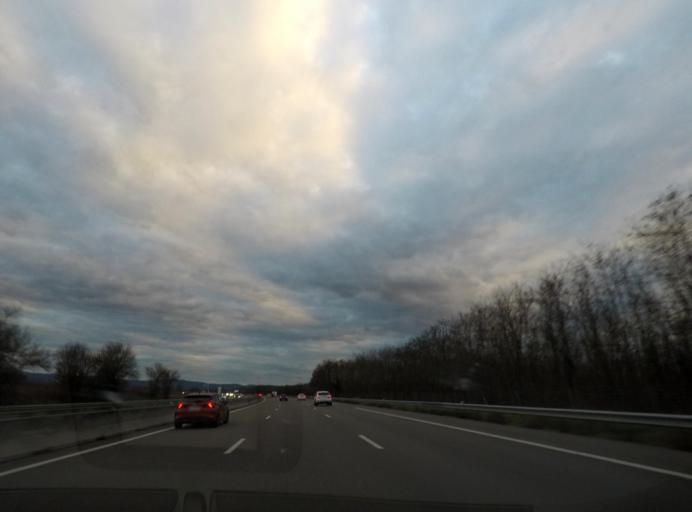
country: FR
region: Rhone-Alpes
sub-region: Departement de l'Ain
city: Saint-Martin-du-Mont
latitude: 46.0848
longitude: 5.2898
